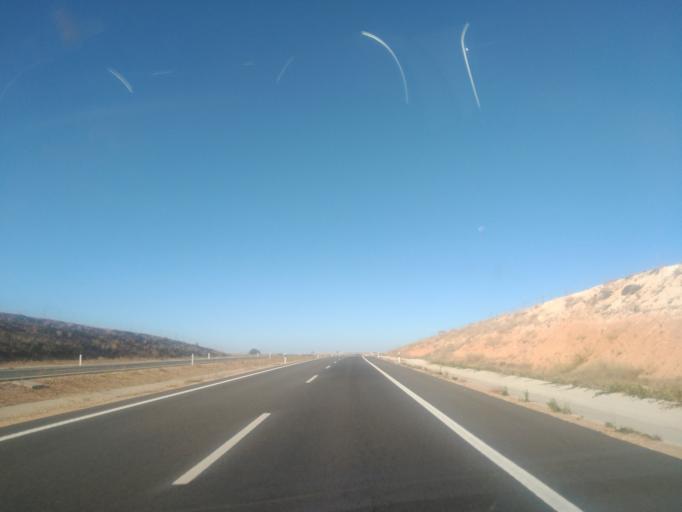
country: ES
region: Castille and Leon
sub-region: Provincia de Burgos
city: Campillo de Aranda
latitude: 41.6332
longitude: -3.7456
